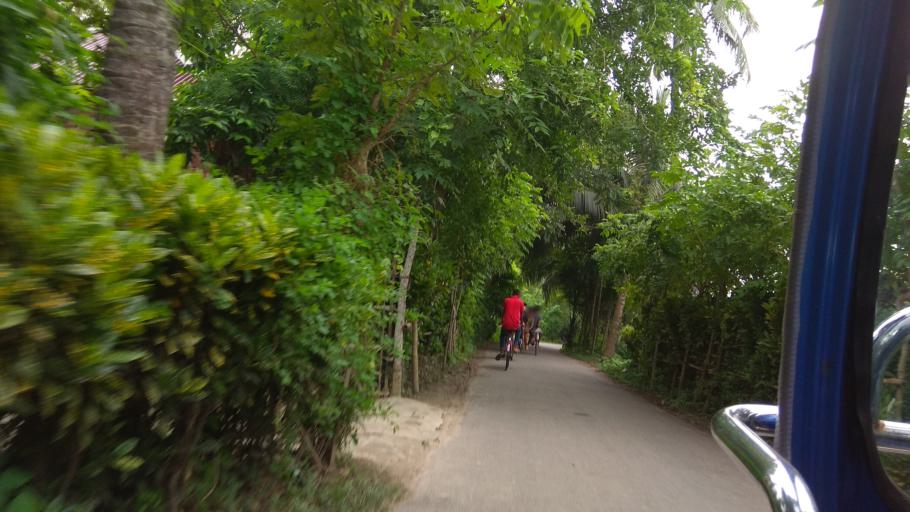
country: BD
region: Khulna
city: Kalia
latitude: 23.0309
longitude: 89.6497
